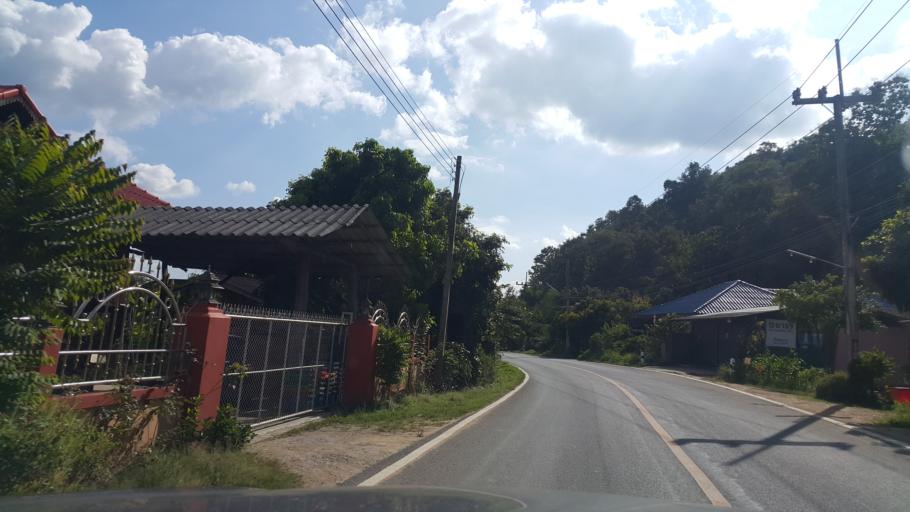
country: TH
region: Lamphun
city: Ban Thi
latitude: 18.5975
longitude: 99.2701
